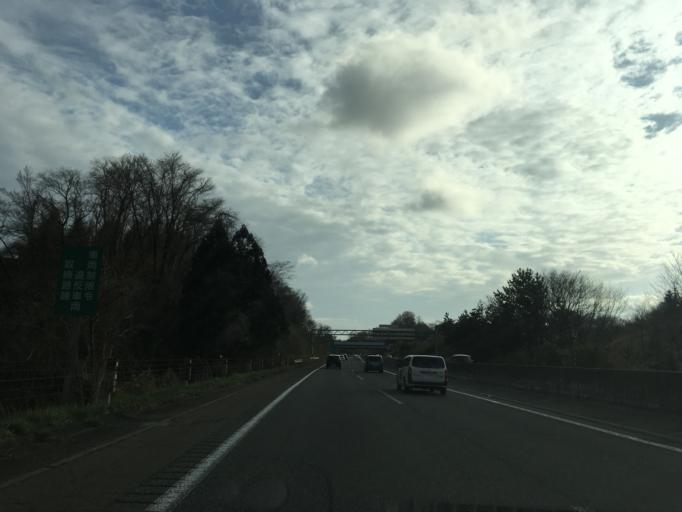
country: JP
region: Miyagi
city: Tomiya
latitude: 38.3679
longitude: 140.8853
